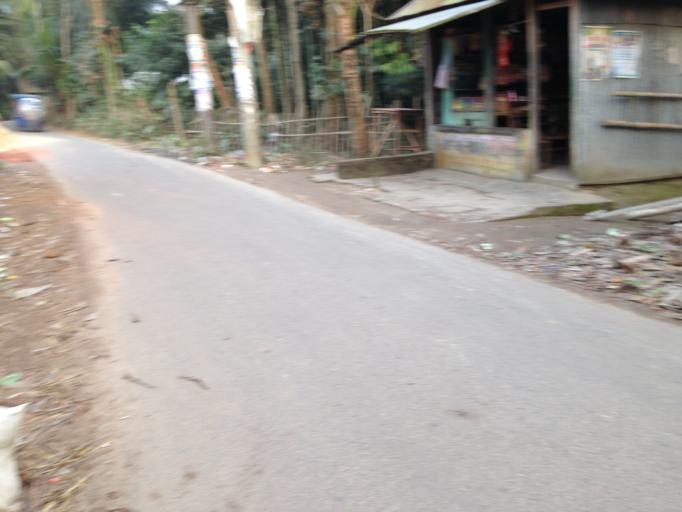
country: BD
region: Chittagong
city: Lakshmipur
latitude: 22.9203
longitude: 90.8378
